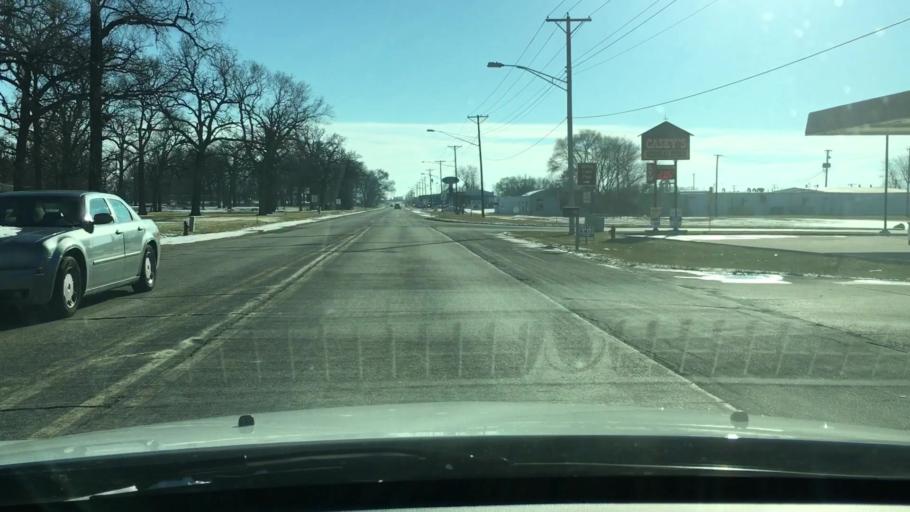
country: US
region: Illinois
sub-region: Ogle County
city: Rochelle
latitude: 41.9169
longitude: -89.0687
